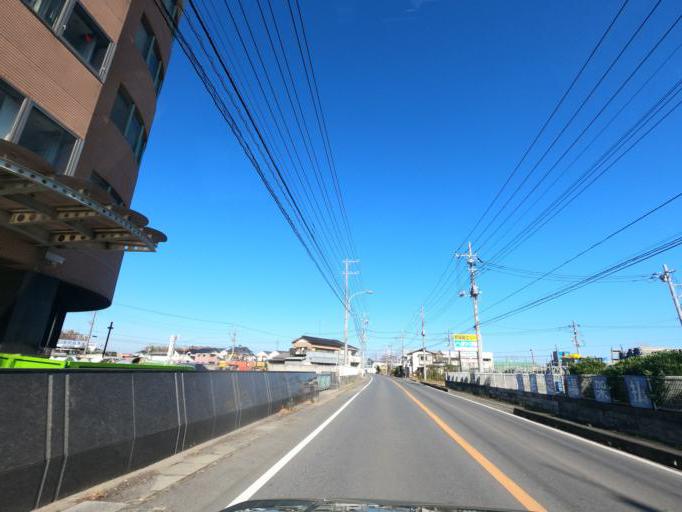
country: JP
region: Ibaraki
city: Mitsukaido
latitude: 36.0111
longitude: 139.9824
